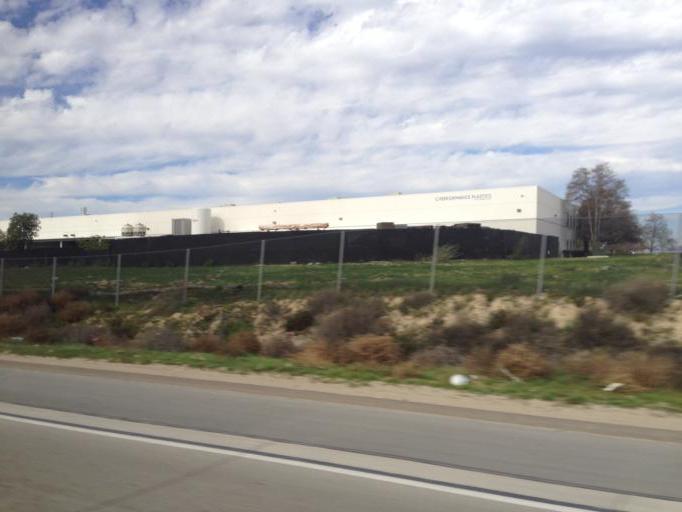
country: MX
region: Baja California
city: Tijuana
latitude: 32.5644
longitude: -116.9709
